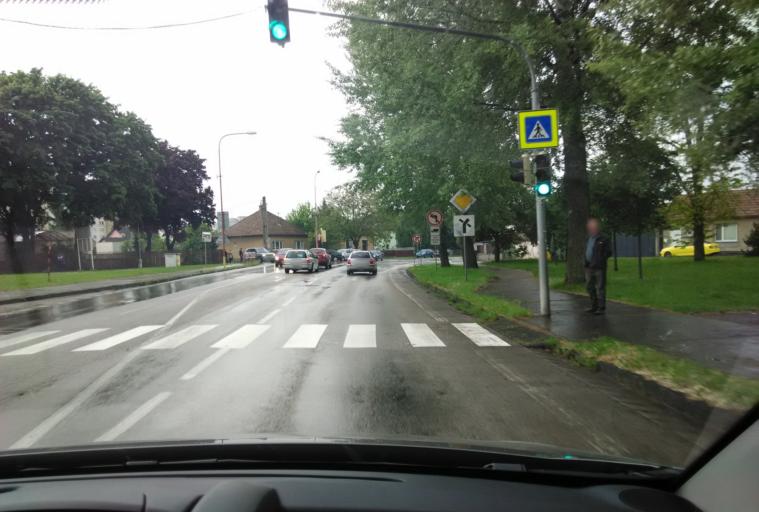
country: SK
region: Trnavsky
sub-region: Okres Trnava
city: Trnava
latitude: 48.3914
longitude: 17.5959
